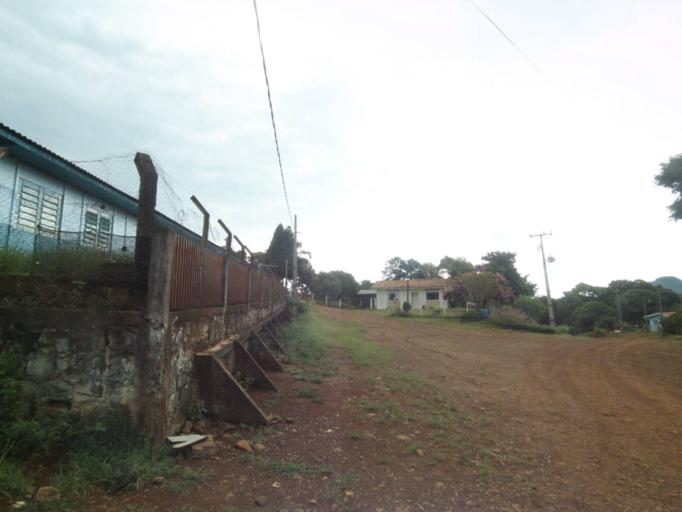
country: BR
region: Parana
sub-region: Pitanga
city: Pitanga
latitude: -24.8988
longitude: -51.9637
